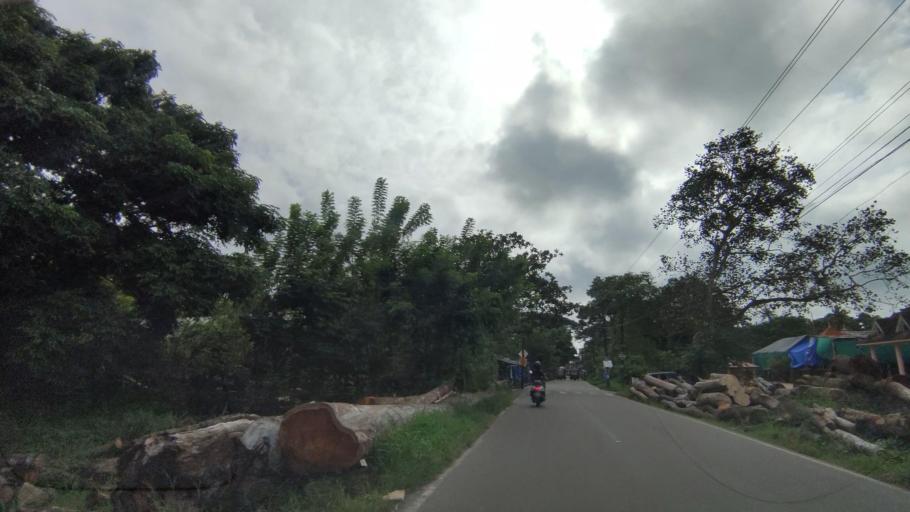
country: IN
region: Kerala
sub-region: Alappuzha
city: Shertallai
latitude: 9.6415
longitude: 76.3555
